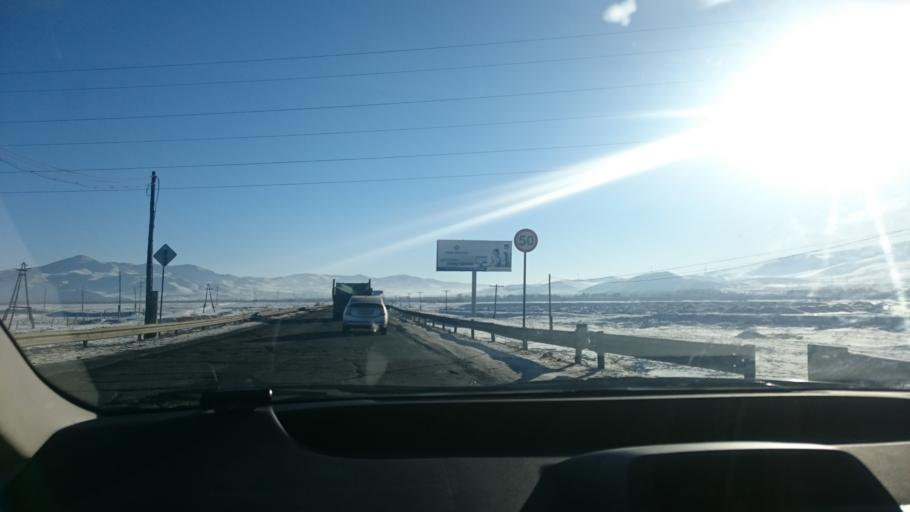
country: MN
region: Ulaanbaatar
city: Ulaanbaatar
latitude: 47.9006
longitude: 107.0346
